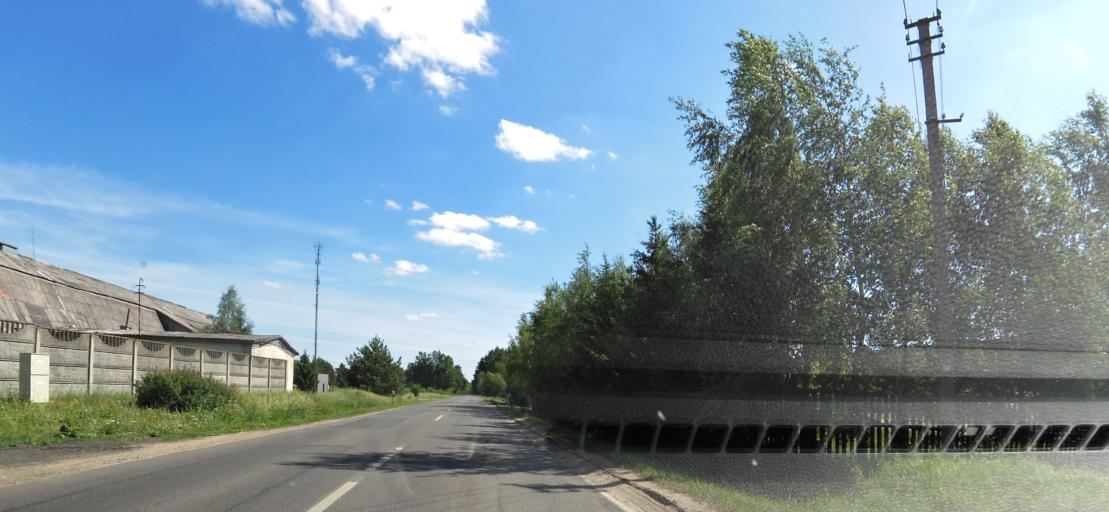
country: LT
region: Vilnius County
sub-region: Vilnius
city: Fabijoniskes
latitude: 54.8000
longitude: 25.3484
